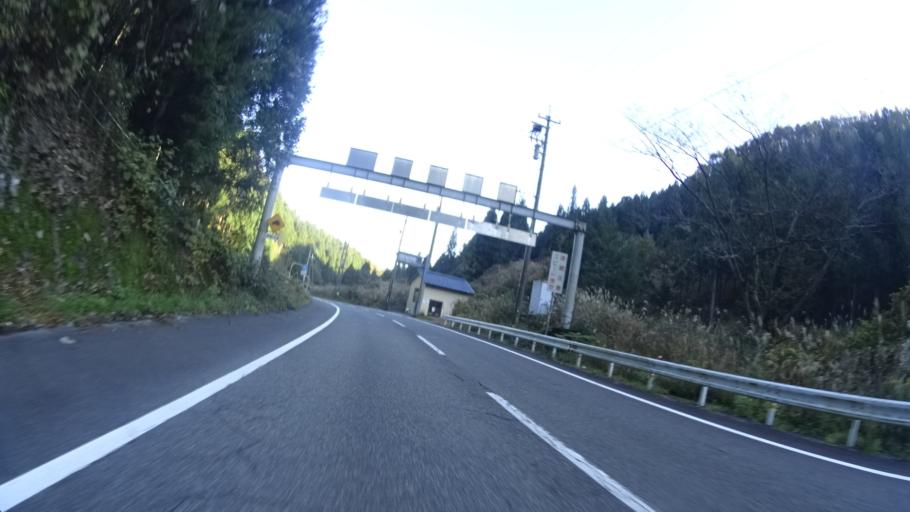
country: JP
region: Fukui
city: Maruoka
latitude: 36.1367
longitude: 136.3248
